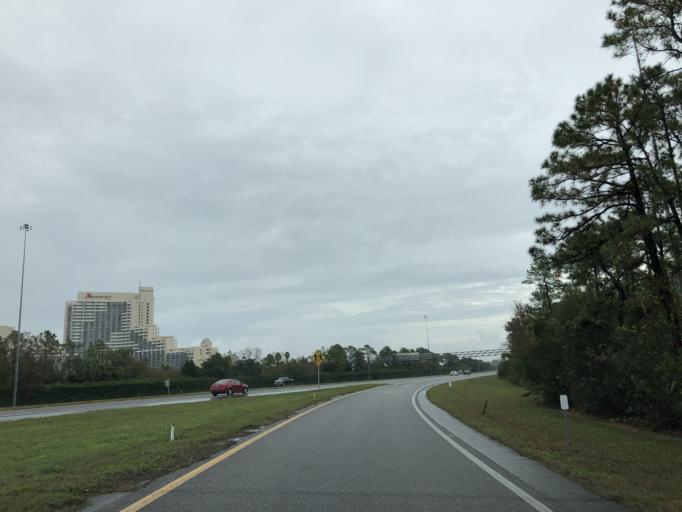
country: US
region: Florida
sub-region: Osceola County
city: Celebration
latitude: 28.3581
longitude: -81.5147
